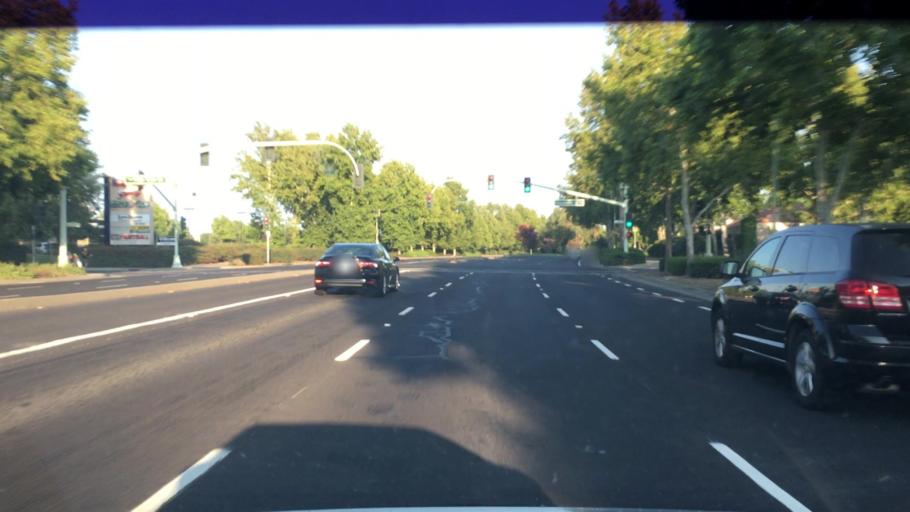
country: US
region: California
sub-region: Sacramento County
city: Laguna
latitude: 38.4274
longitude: -121.4663
